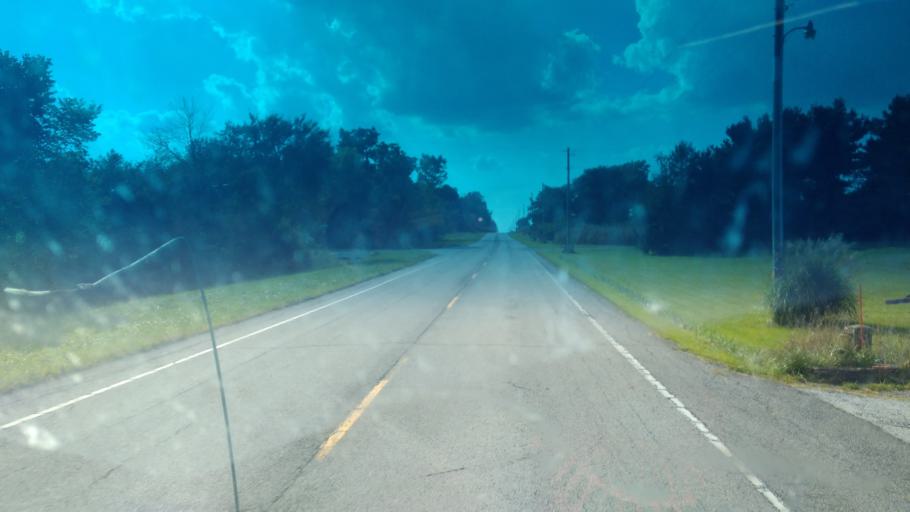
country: US
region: Ohio
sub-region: Hardin County
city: Forest
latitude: 40.8334
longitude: -83.5752
